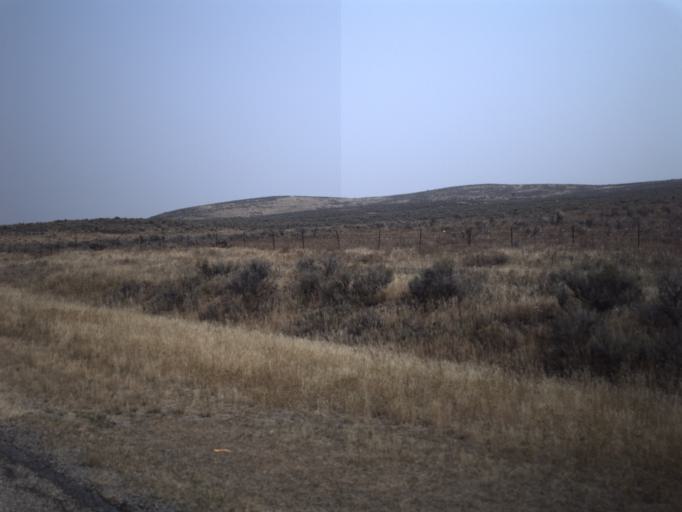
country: US
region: Utah
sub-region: Morgan County
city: Morgan
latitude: 40.9525
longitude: -111.5496
